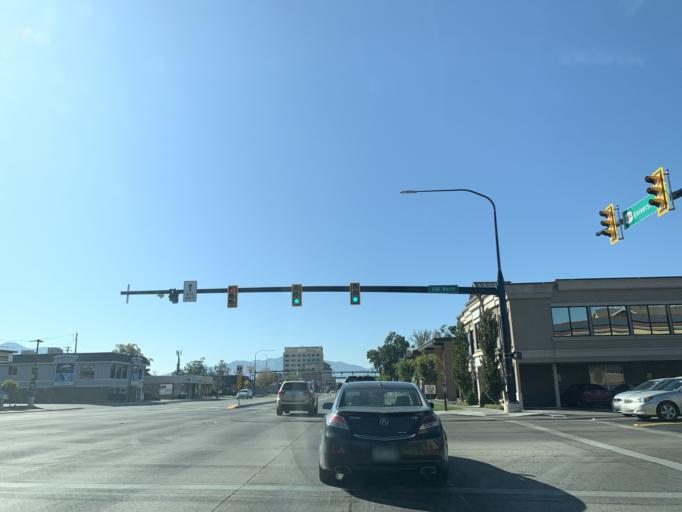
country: US
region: Utah
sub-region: Utah County
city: Provo
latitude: 40.2406
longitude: -111.6588
